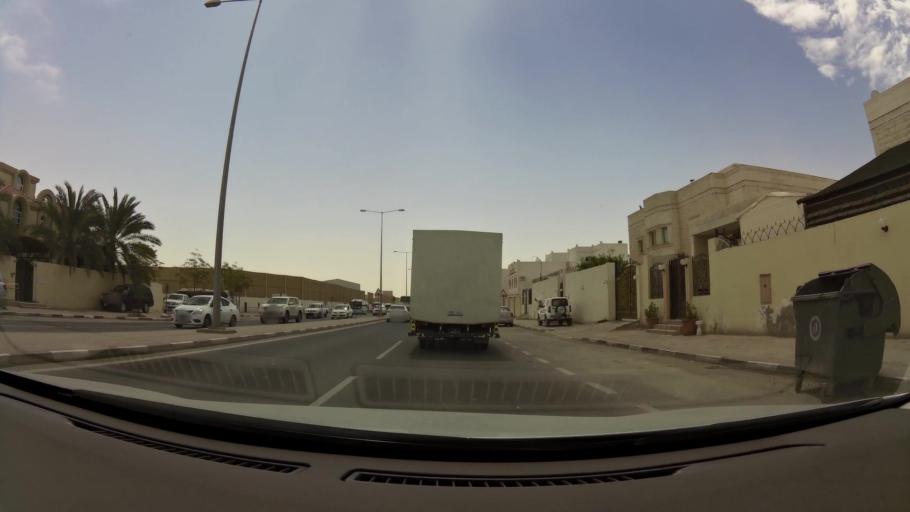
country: QA
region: Baladiyat ar Rayyan
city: Ar Rayyan
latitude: 25.2569
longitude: 51.4183
